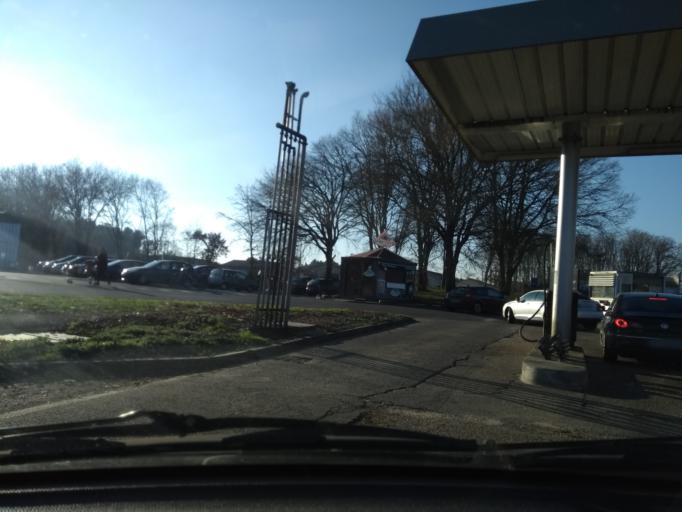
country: FR
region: Aquitaine
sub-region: Departement de la Gironde
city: Salles
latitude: 44.5473
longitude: -0.8743
